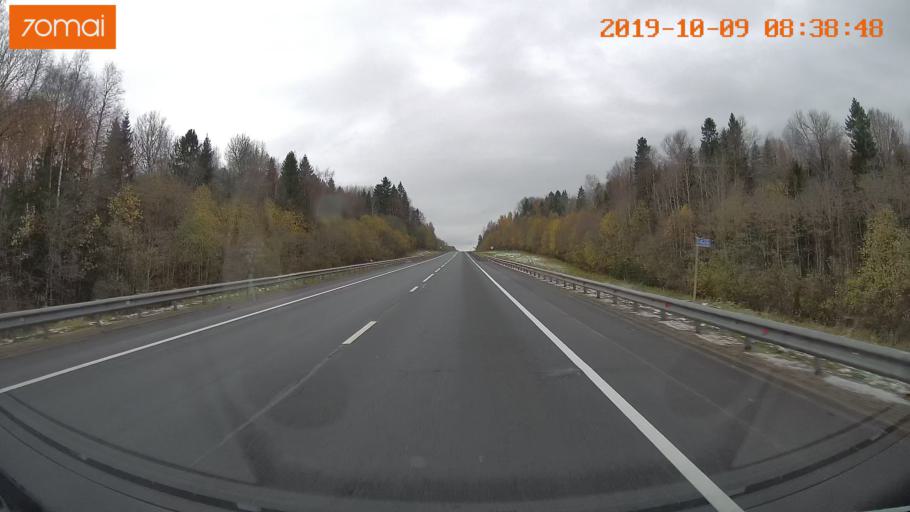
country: RU
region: Vologda
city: Gryazovets
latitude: 58.9620
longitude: 40.1611
